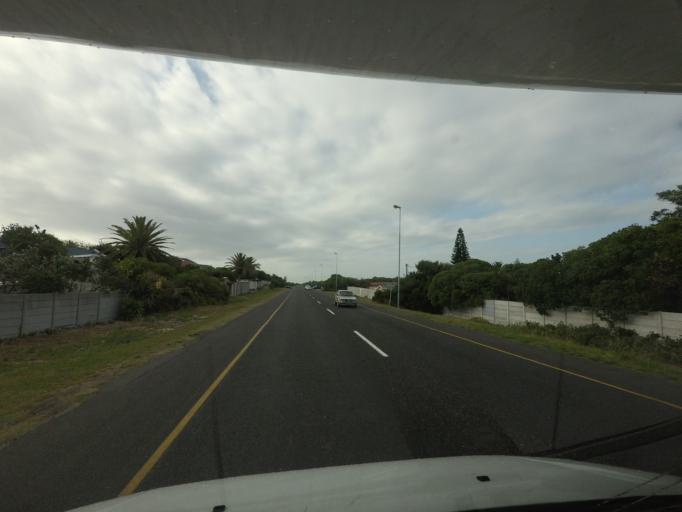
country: ZA
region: Western Cape
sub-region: City of Cape Town
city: Sunset Beach
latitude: -33.7184
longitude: 18.4460
